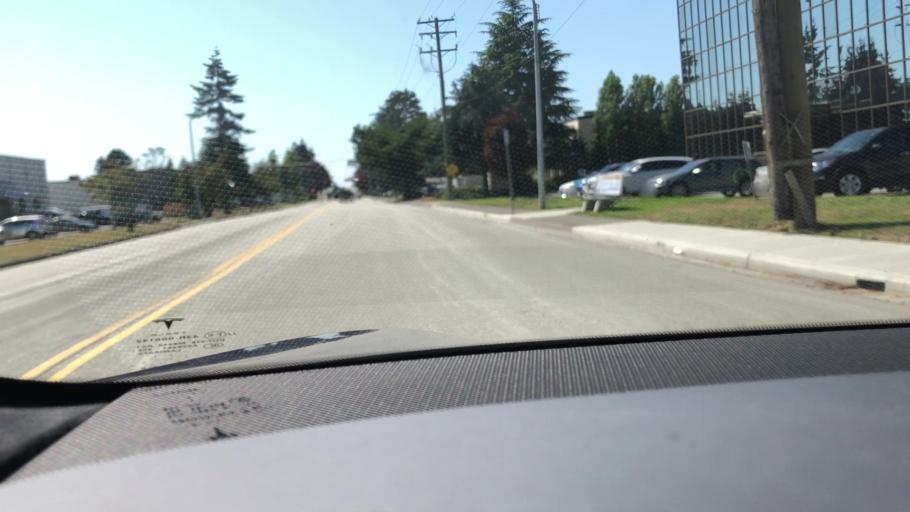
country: CA
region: British Columbia
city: Richmond
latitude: 49.1923
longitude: -123.0698
